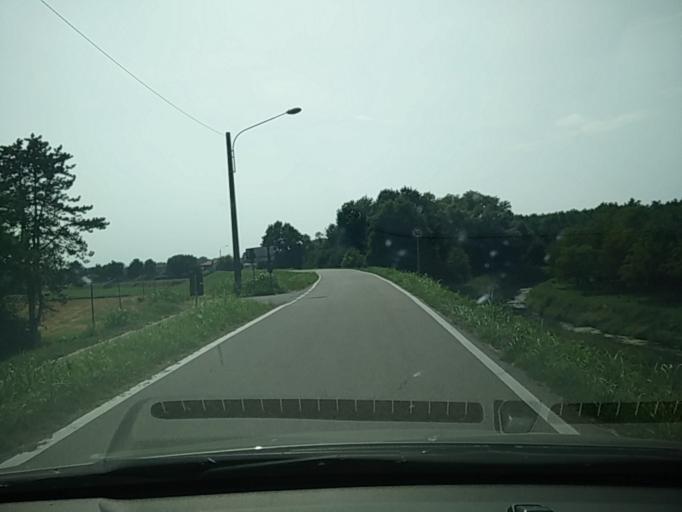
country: IT
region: Lombardy
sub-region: Provincia di Pavia
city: Rotta
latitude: 45.1710
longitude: 9.1628
